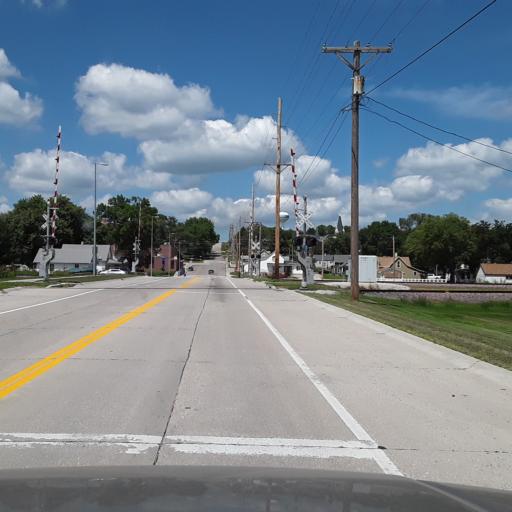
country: US
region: Nebraska
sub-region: Nance County
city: Genoa
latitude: 41.4466
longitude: -97.7346
